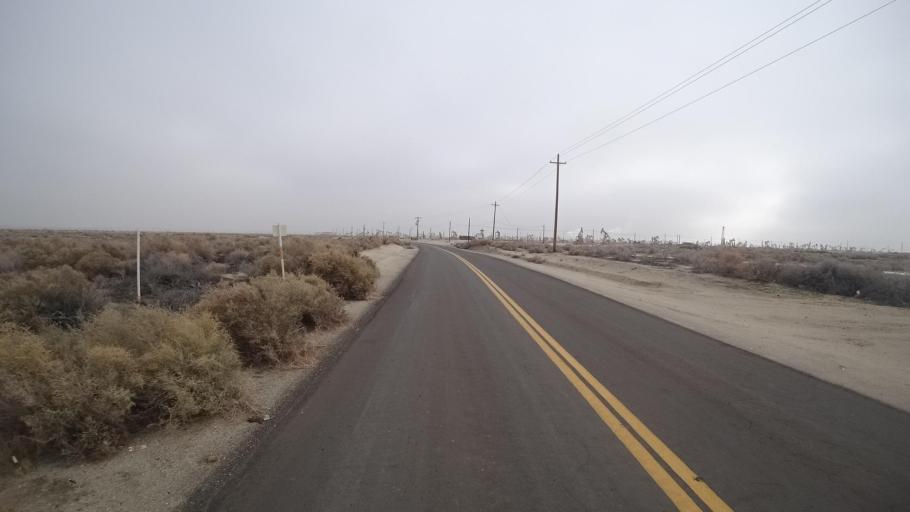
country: US
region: California
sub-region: Kern County
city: Maricopa
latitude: 35.0841
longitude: -119.3940
